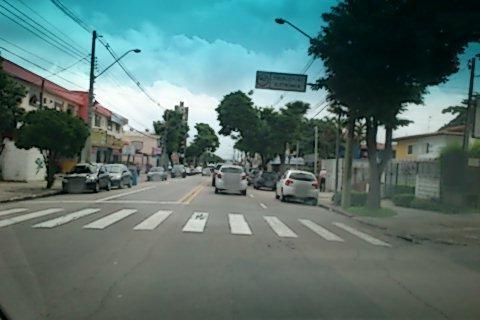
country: BR
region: Sao Paulo
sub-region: Sao Jose Dos Campos
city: Sao Jose dos Campos
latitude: -23.2295
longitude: -45.8825
